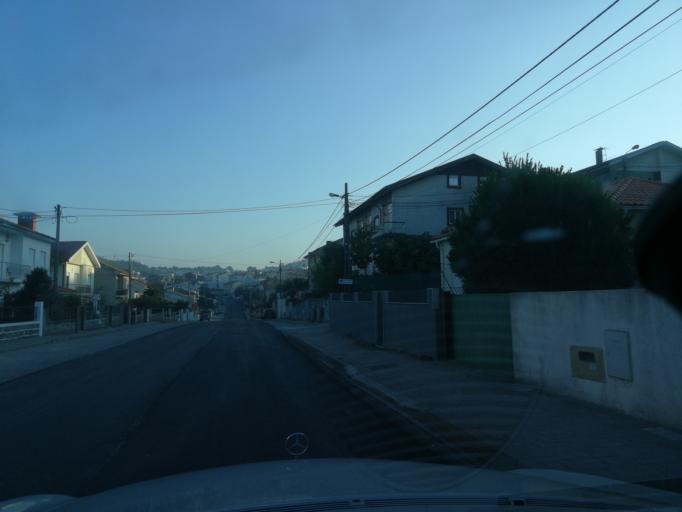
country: PT
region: Braga
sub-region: Braga
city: Braga
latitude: 41.5244
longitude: -8.4300
